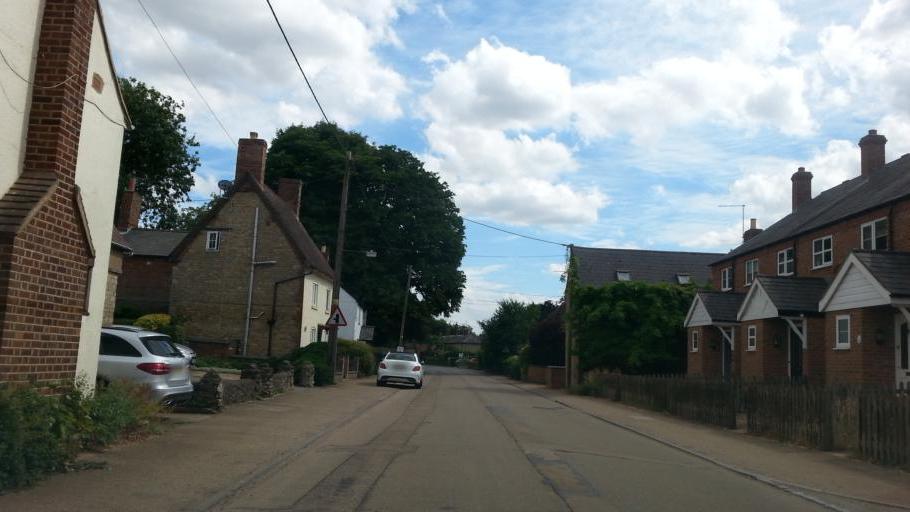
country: GB
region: England
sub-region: Northamptonshire
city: Silverstone
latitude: 52.0866
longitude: -0.9917
